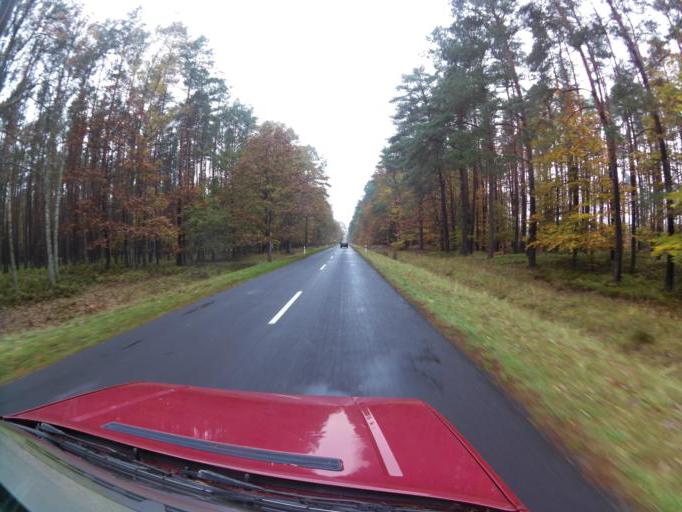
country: PL
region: West Pomeranian Voivodeship
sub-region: Powiat policki
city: Dobra
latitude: 53.5719
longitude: 14.4345
